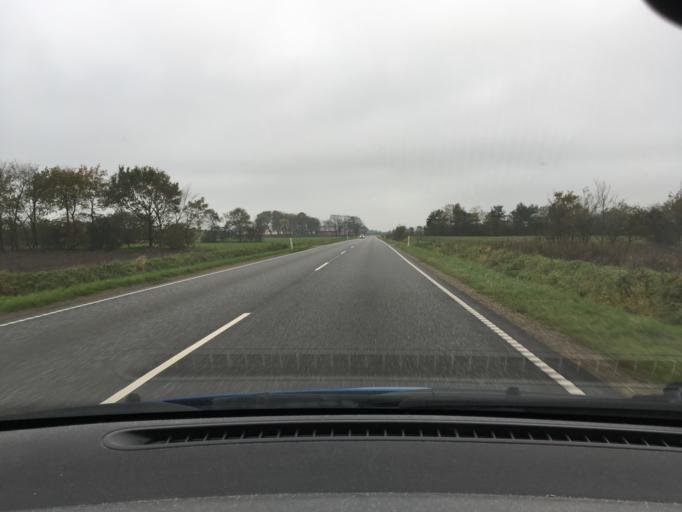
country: DK
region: South Denmark
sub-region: Tonder Kommune
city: Toftlund
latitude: 55.0628
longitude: 9.1451
